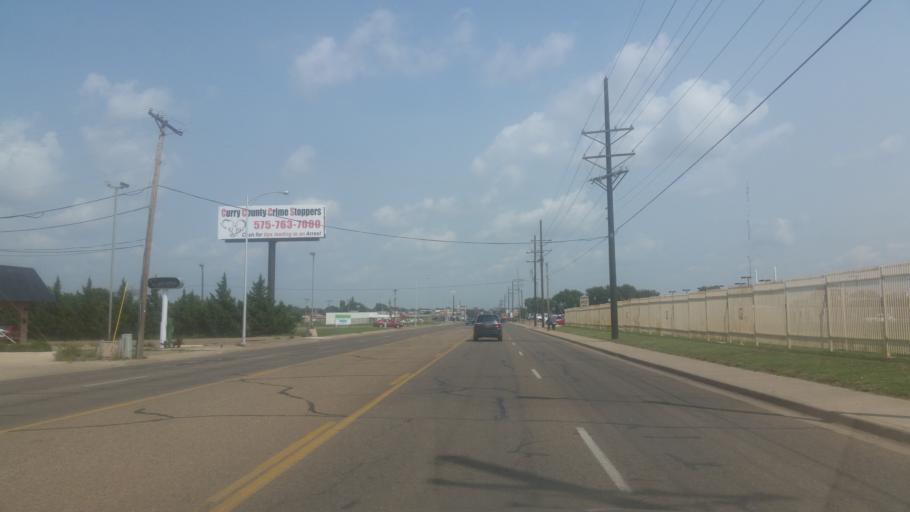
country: US
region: New Mexico
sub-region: Curry County
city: Clovis
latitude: 34.4192
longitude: -103.2180
